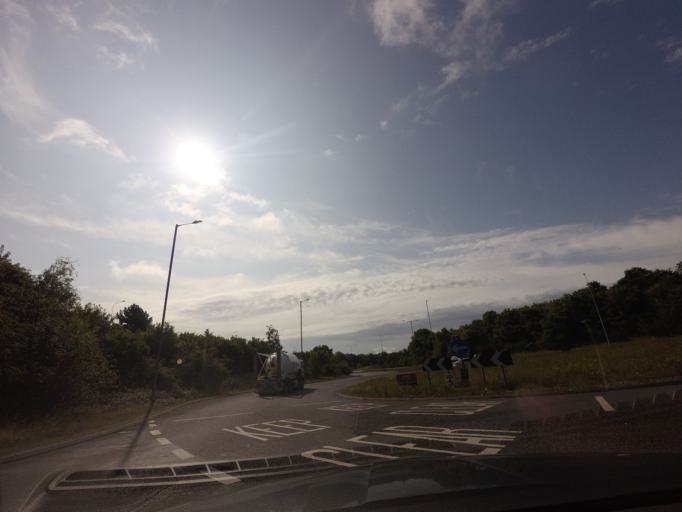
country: GB
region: England
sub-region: Kent
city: Harrietsham
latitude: 51.2613
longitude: 0.6127
